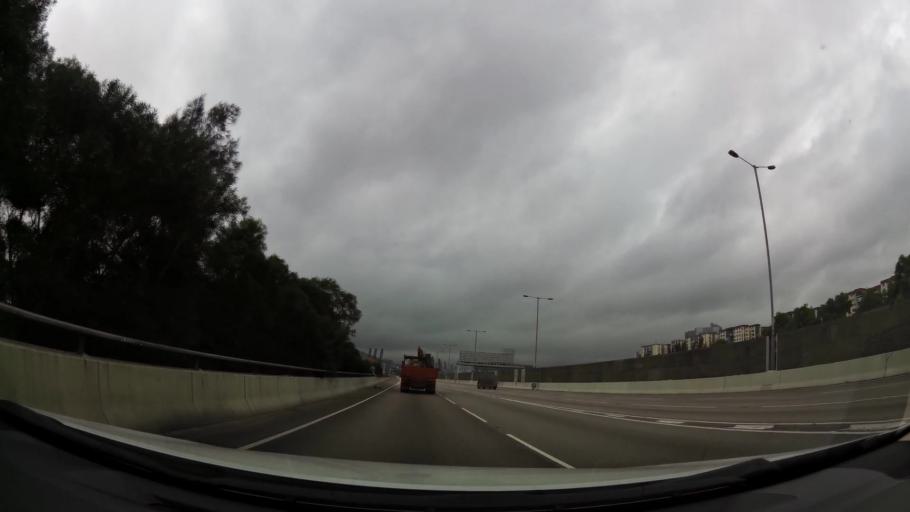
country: HK
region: Sham Shui Po
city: Sham Shui Po
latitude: 22.3327
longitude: 114.1395
